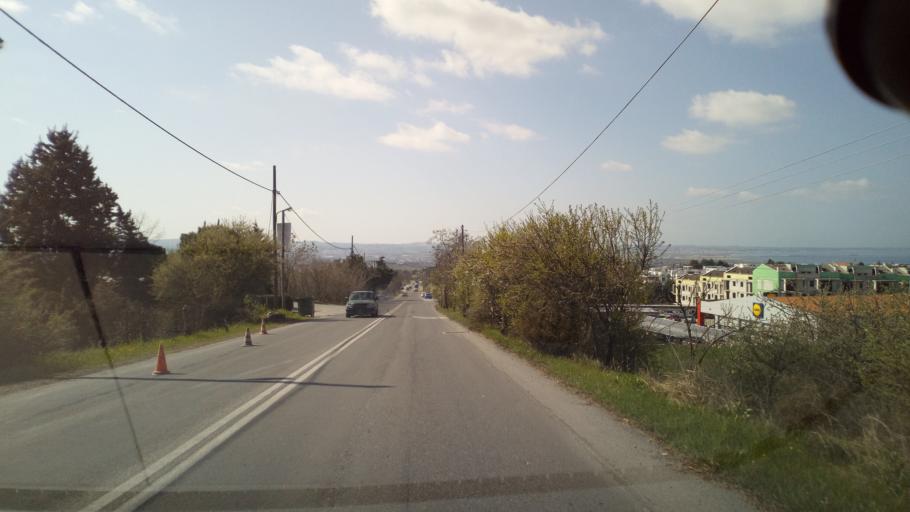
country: GR
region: Central Macedonia
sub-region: Nomos Thessalonikis
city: Thermi
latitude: 40.5615
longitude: 23.0232
